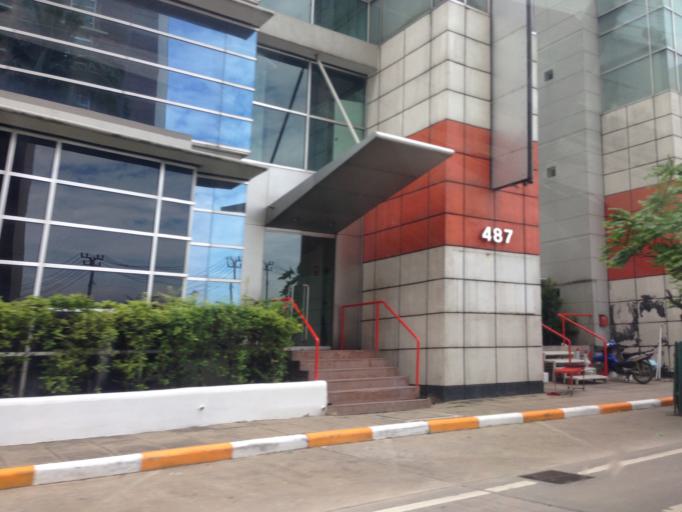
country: TH
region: Nonthaburi
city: Pak Kret
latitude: 13.9279
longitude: 100.5326
